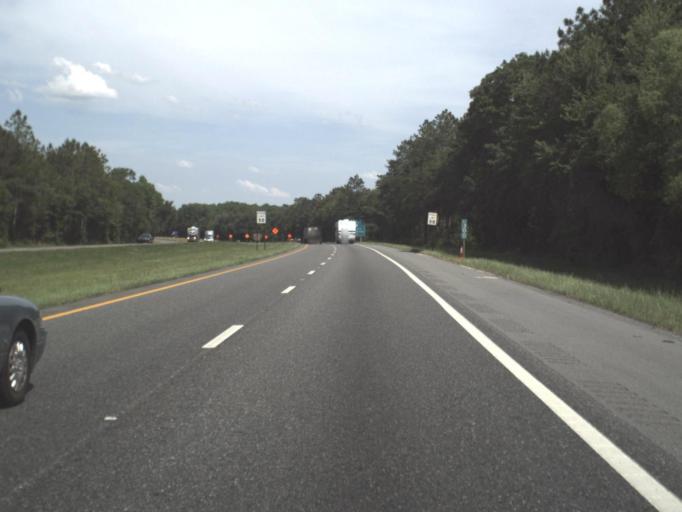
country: US
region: Florida
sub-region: Columbia County
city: Five Points
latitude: 30.2463
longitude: -82.6970
